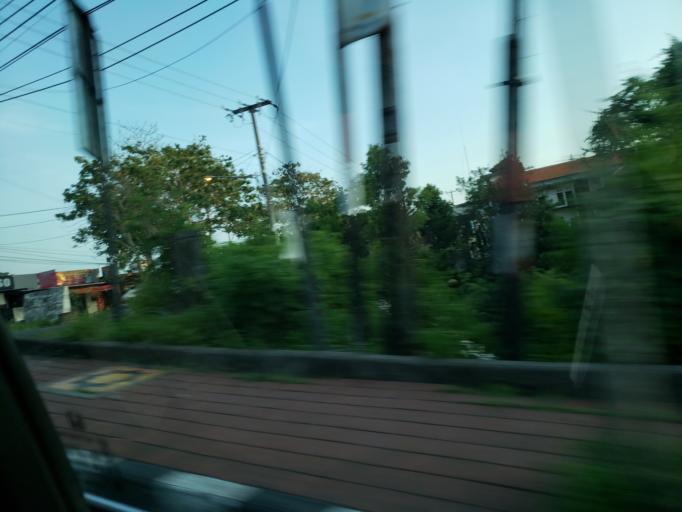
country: ID
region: Bali
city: Jimbaran
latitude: -8.7998
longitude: 115.1666
